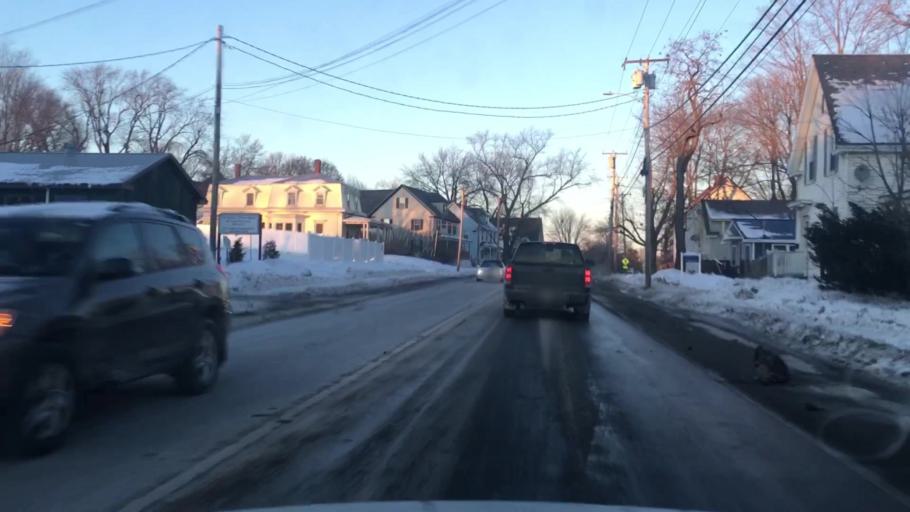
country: US
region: Maine
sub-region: Penobscot County
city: Bangor
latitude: 44.7750
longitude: -68.7792
